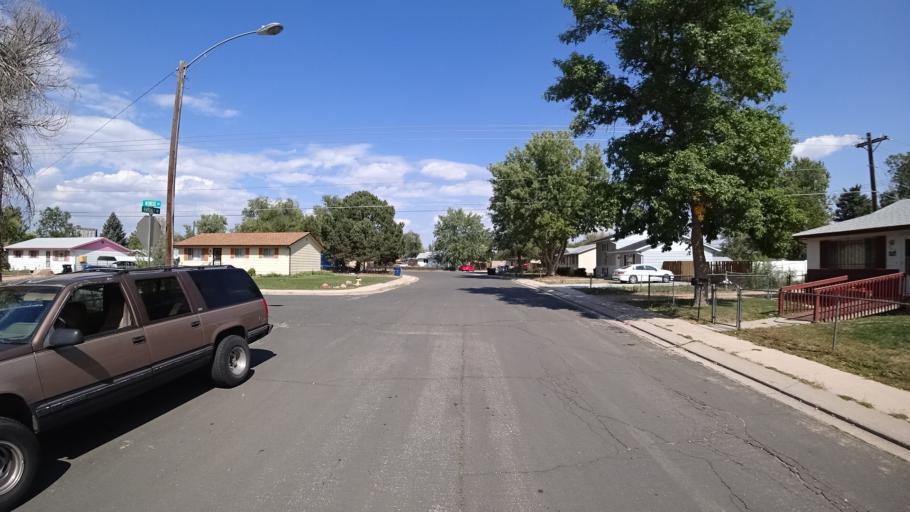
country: US
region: Colorado
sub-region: El Paso County
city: Colorado Springs
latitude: 38.8197
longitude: -104.7845
